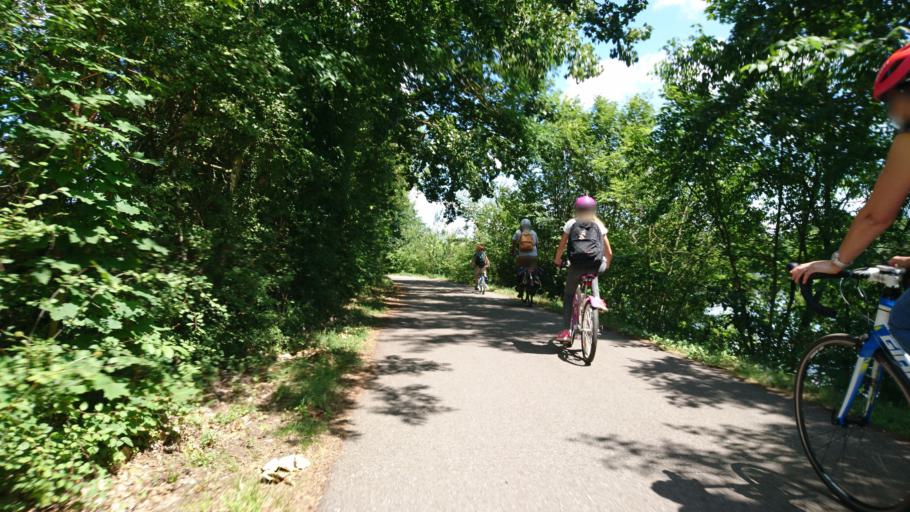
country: FR
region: Lorraine
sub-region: Departement de la Moselle
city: Longeville-les-Metz
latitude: 49.1065
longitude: 6.1398
